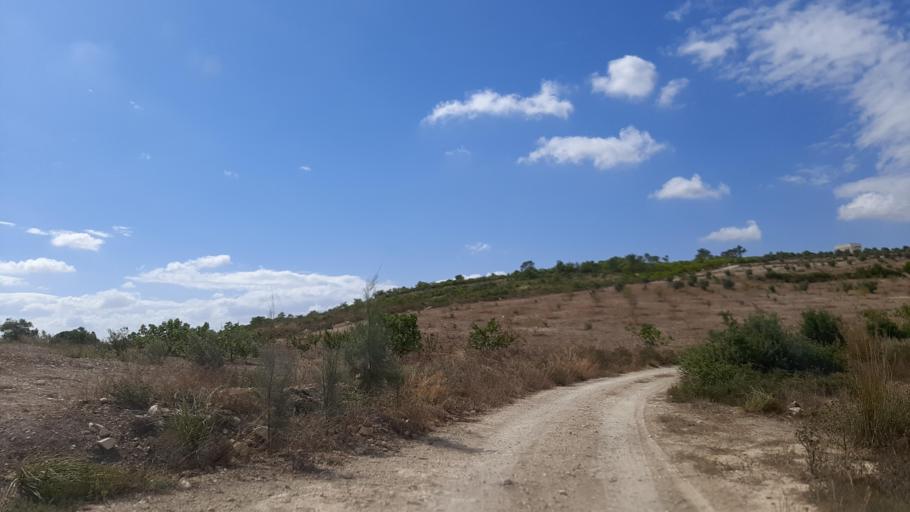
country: TN
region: Zaghwan
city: Zaghouan
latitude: 36.4995
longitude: 10.1763
